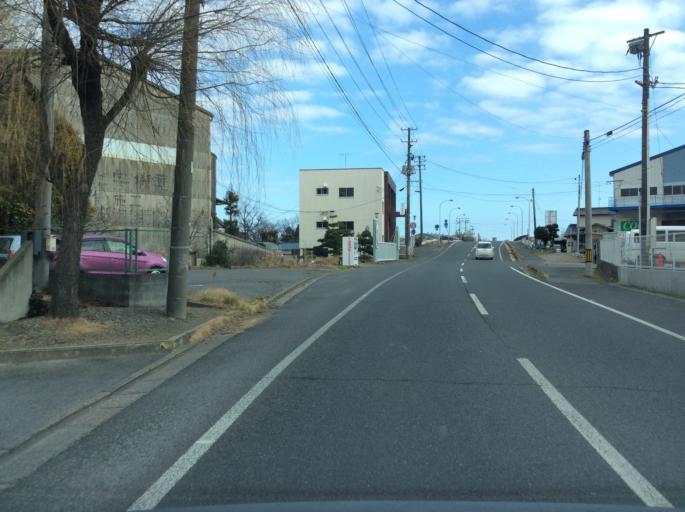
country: JP
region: Fukushima
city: Iwaki
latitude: 36.9527
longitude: 140.8757
